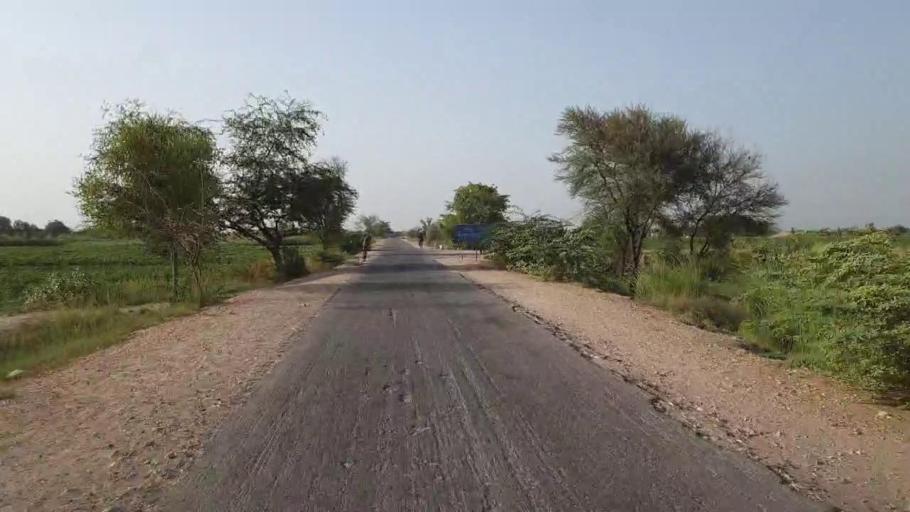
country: PK
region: Sindh
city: Jam Sahib
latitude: 26.4671
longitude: 68.8590
